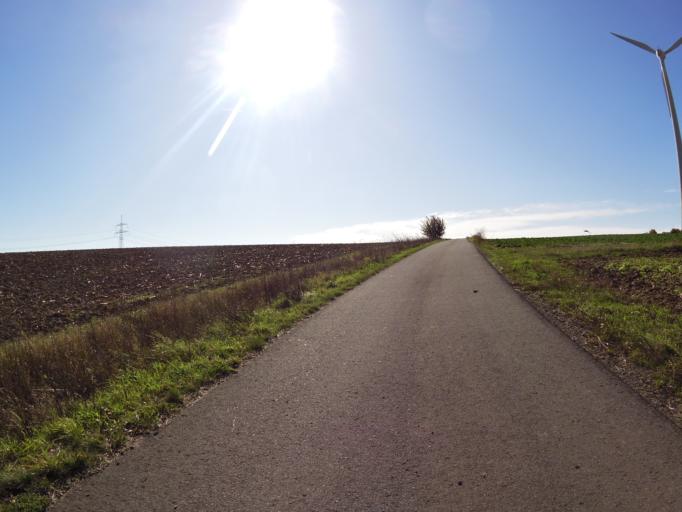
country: DE
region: Bavaria
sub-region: Regierungsbezirk Unterfranken
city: Theilheim
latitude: 49.7505
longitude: 10.0463
